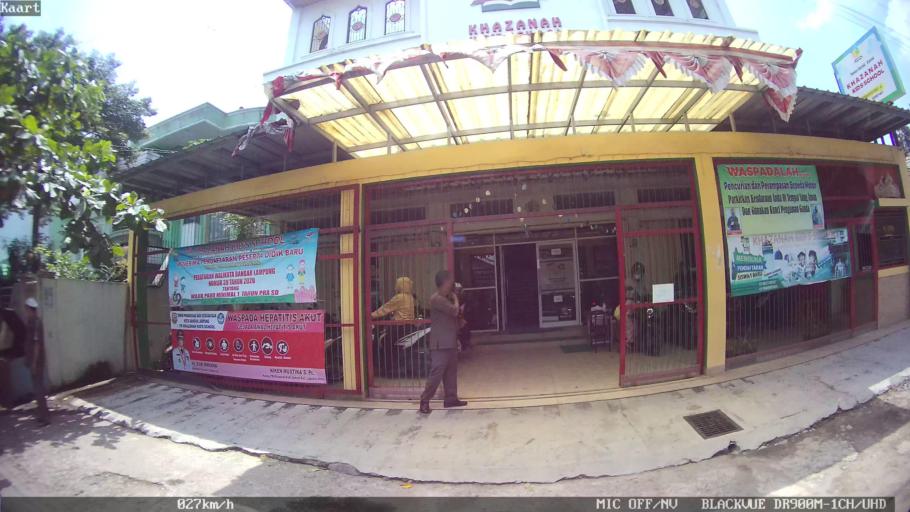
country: ID
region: Lampung
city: Kedaton
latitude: -5.3745
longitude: 105.2661
